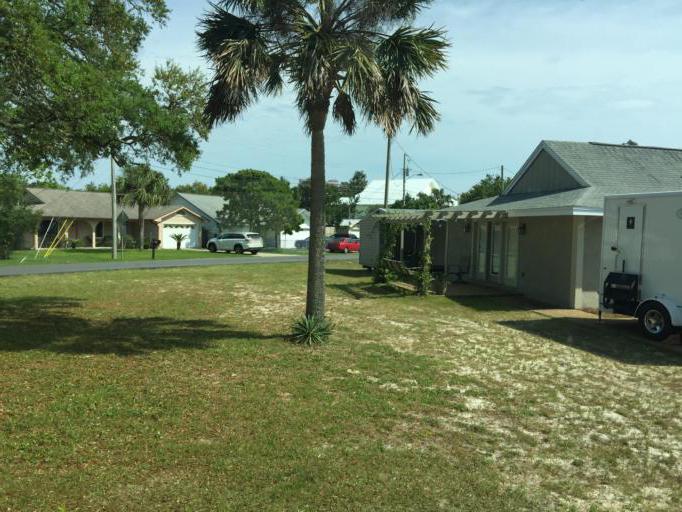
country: US
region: Florida
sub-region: Bay County
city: Laguna Beach
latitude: 30.2212
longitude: -85.8795
